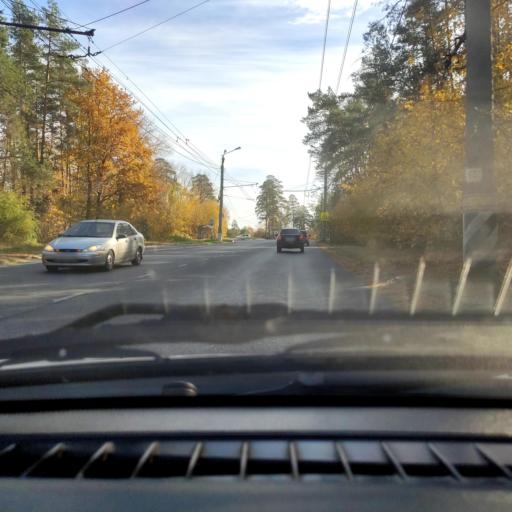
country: RU
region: Samara
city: Tol'yatti
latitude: 53.4786
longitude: 49.3561
